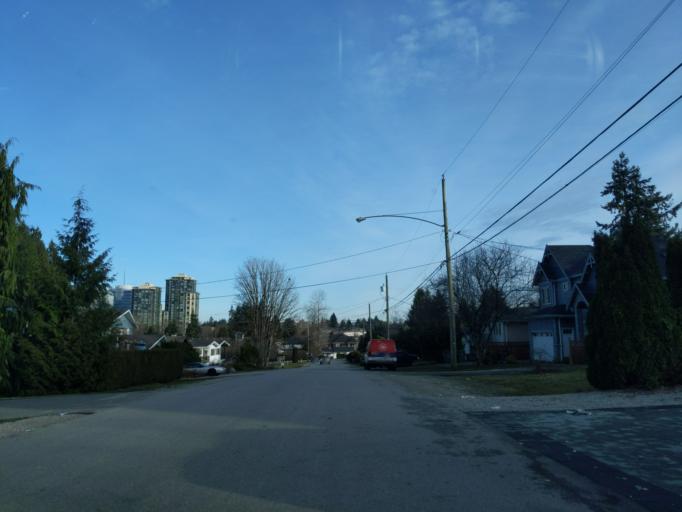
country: CA
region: British Columbia
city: New Westminster
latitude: 49.1970
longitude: -122.8592
